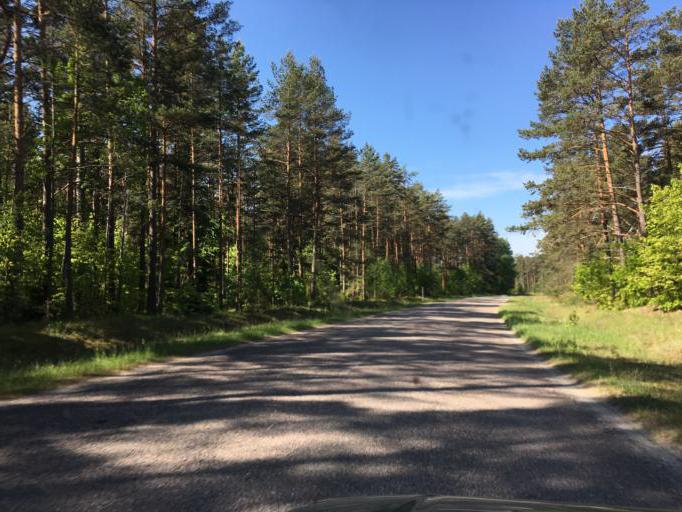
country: LV
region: Ventspils
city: Ventspils
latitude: 57.5157
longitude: 21.8816
